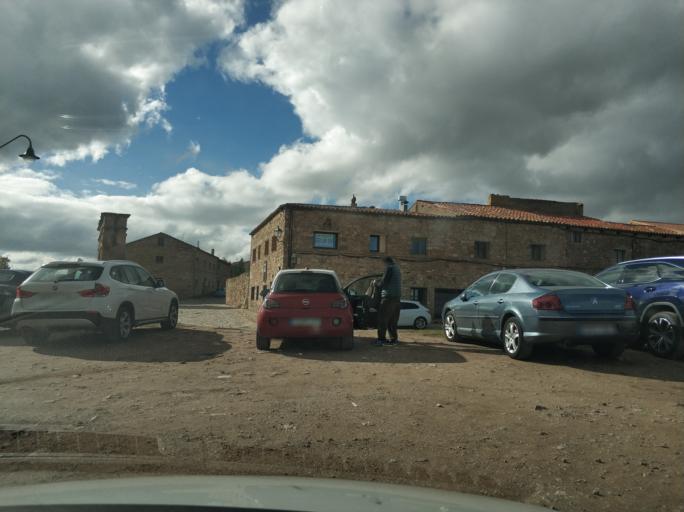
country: ES
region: Castille and Leon
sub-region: Provincia de Soria
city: Medinaceli
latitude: 41.1712
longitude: -2.4319
